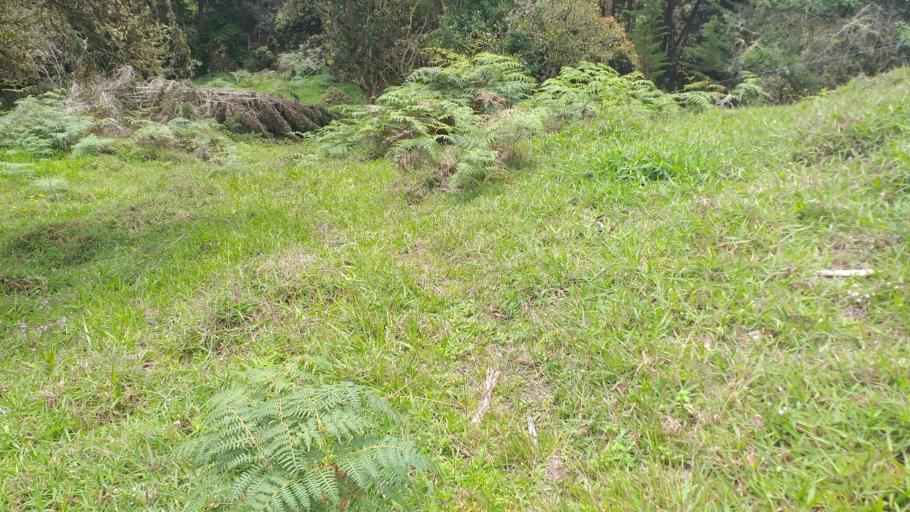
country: CO
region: Cundinamarca
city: Tenza
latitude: 5.0724
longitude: -73.4572
